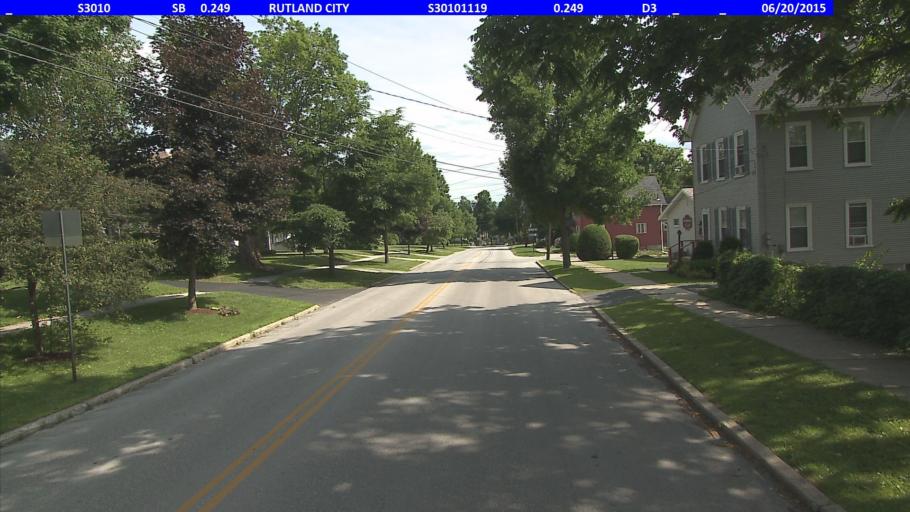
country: US
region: Vermont
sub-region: Rutland County
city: Rutland
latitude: 43.6064
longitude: -72.9684
